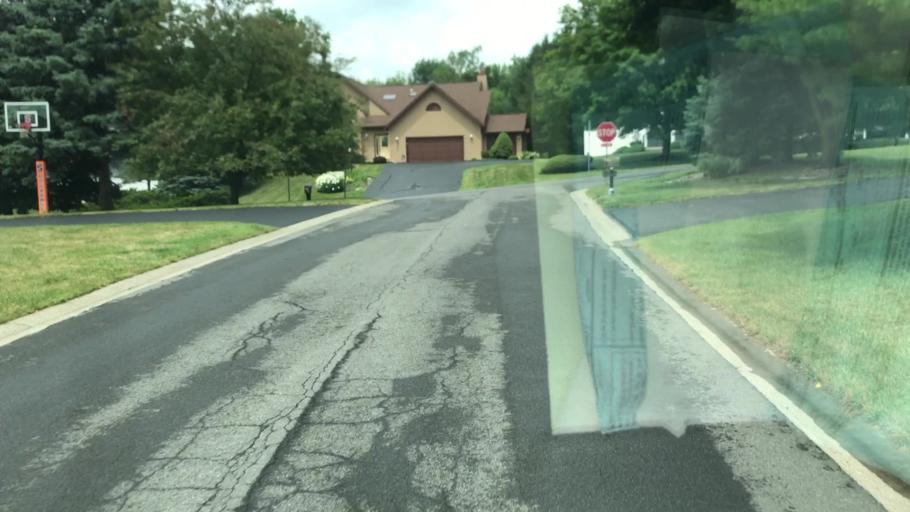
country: US
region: New York
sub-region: Onondaga County
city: Manlius
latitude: 42.9898
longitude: -75.9798
